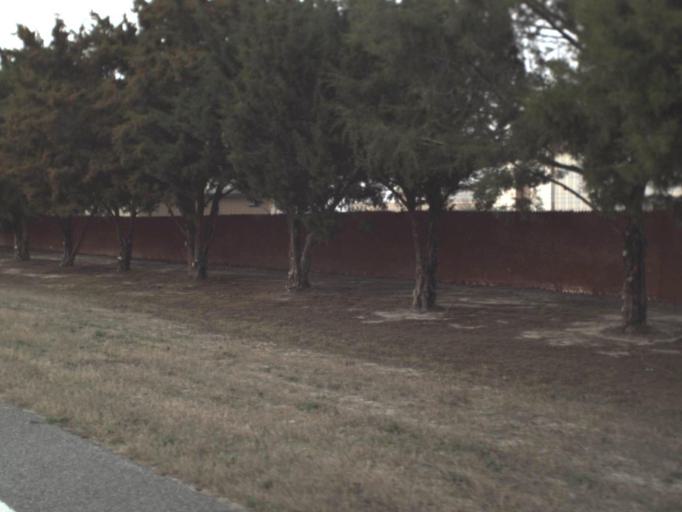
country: US
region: Florida
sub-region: Bay County
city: Tyndall Air Force Base
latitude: 30.0661
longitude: -85.5852
